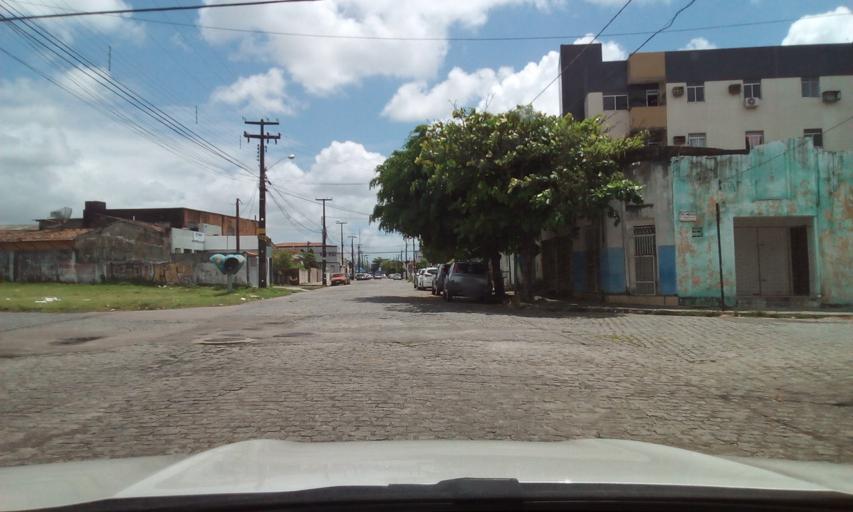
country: BR
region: Paraiba
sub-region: Joao Pessoa
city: Joao Pessoa
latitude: -7.1372
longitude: -34.8775
